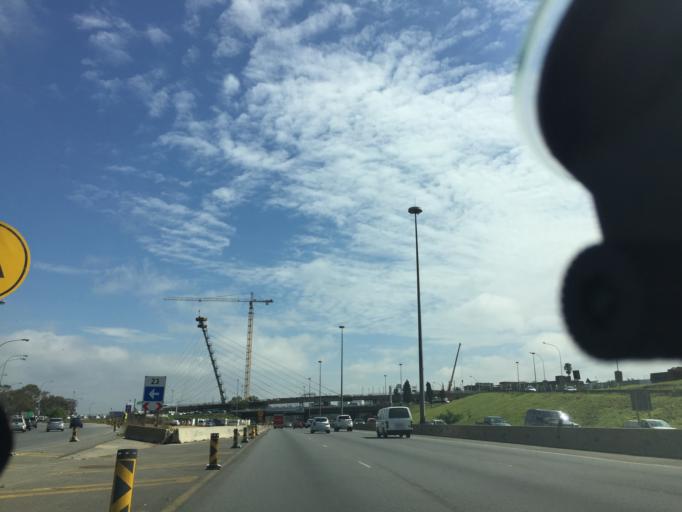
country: ZA
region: Gauteng
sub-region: City of Johannesburg Metropolitan Municipality
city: Modderfontein
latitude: -26.1110
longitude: 28.0760
